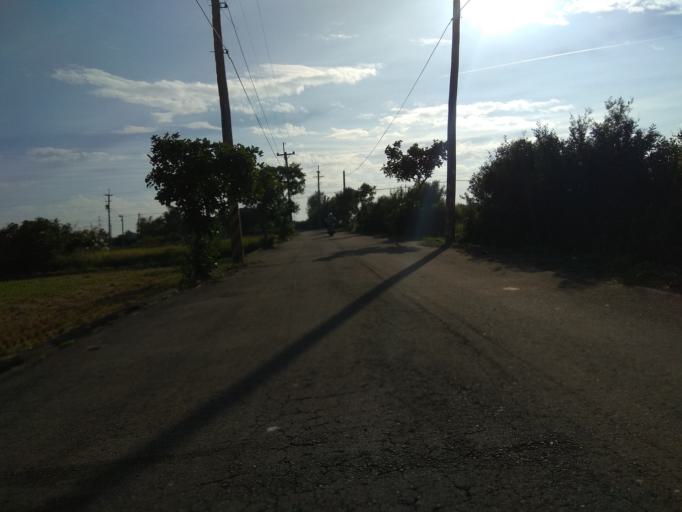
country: TW
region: Taiwan
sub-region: Hsinchu
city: Zhubei
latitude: 24.9811
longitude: 121.0575
